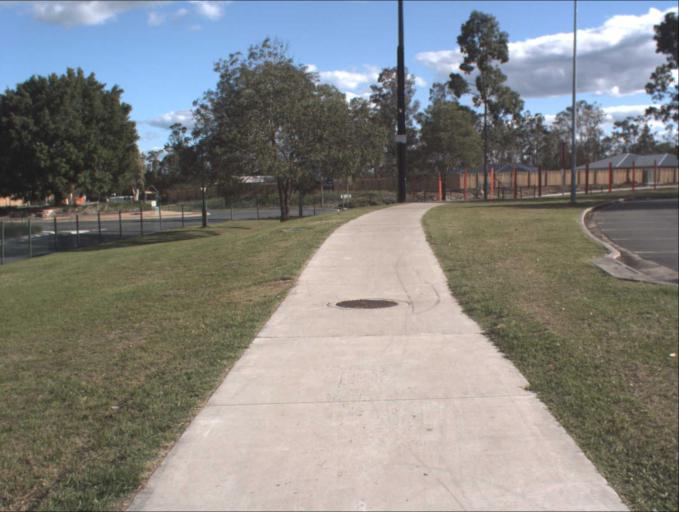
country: AU
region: Queensland
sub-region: Logan
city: North Maclean
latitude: -27.8086
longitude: 152.9558
